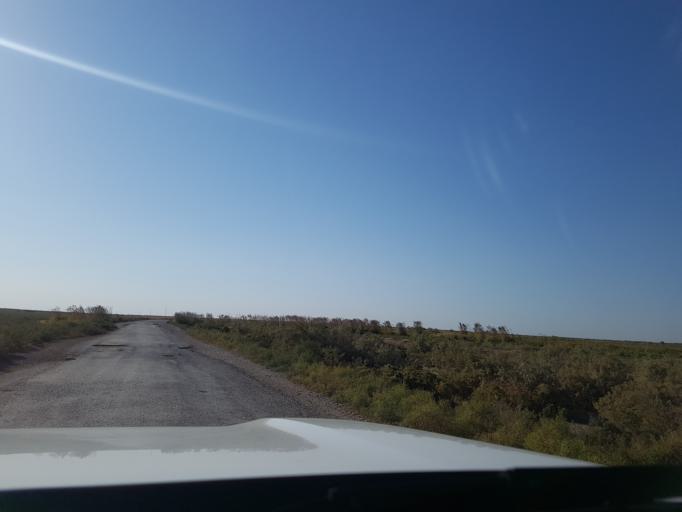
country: IR
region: Razavi Khorasan
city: Sarakhs
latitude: 36.9968
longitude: 61.3842
